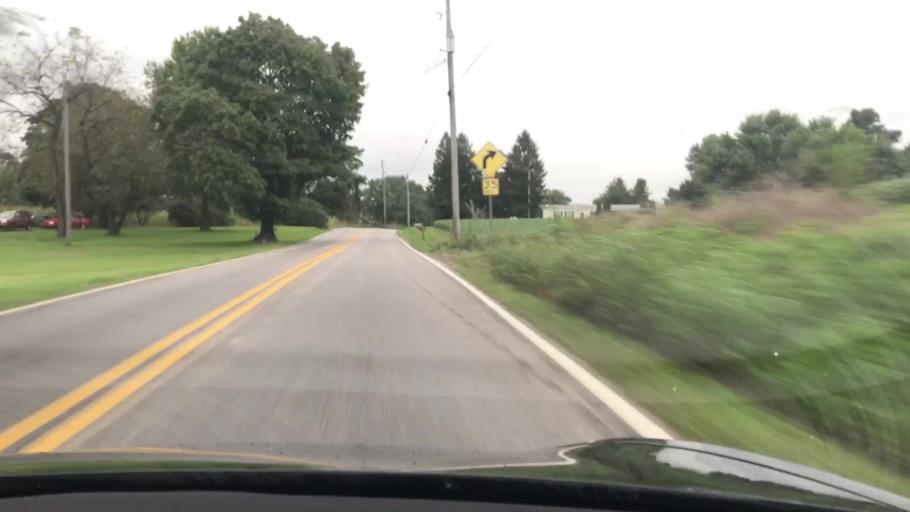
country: US
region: Pennsylvania
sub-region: York County
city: Dover
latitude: 39.9597
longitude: -76.8691
